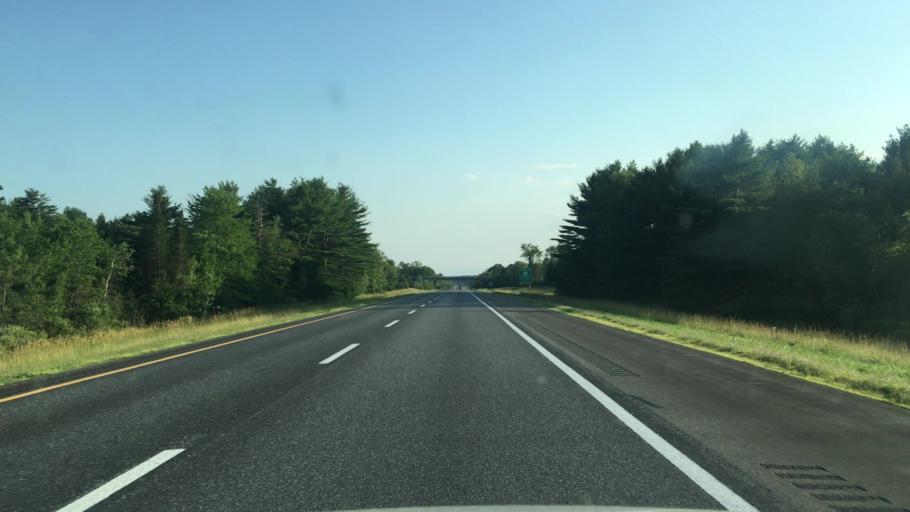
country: US
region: Maine
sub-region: Sagadahoc County
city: Richmond
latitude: 44.1179
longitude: -69.8546
